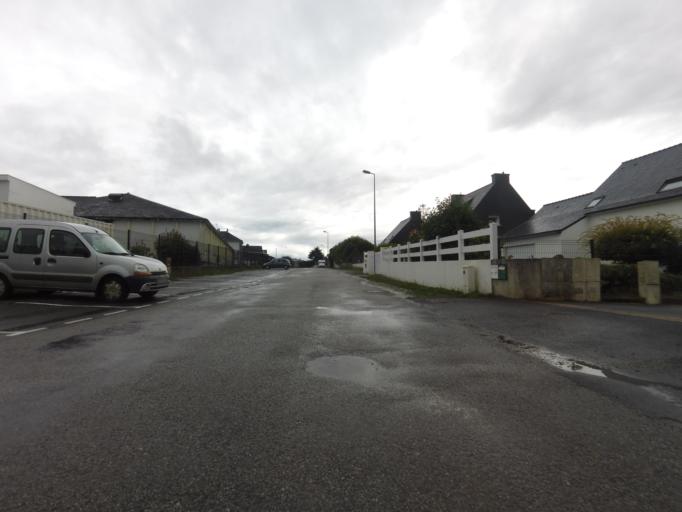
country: FR
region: Brittany
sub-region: Departement du Morbihan
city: Etel
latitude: 47.6639
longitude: -3.2047
